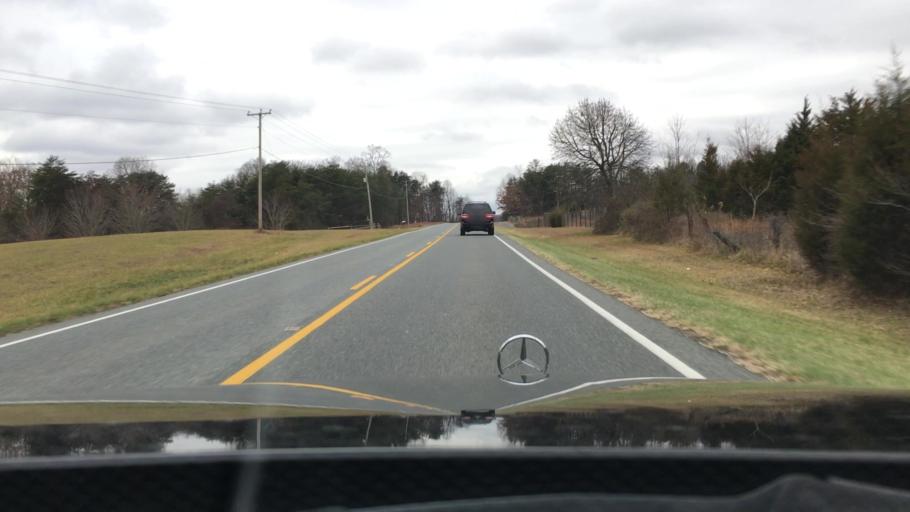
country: US
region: Virginia
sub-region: Franklin County
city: North Shore
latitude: 37.2433
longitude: -79.6769
